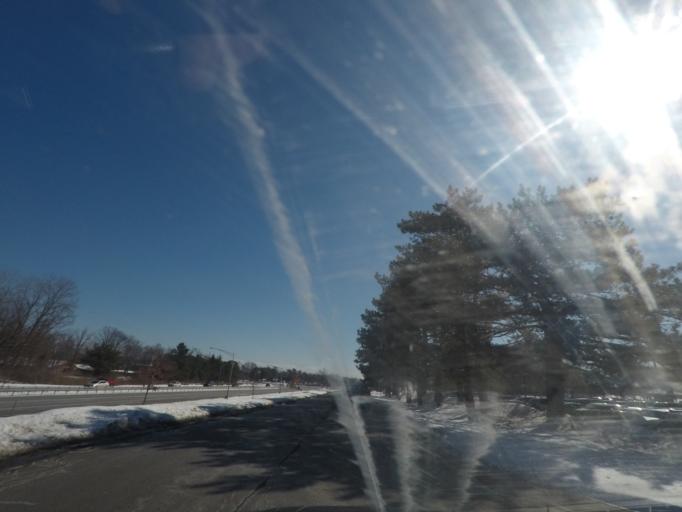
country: US
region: New York
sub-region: Albany County
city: Westmere
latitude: 42.7032
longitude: -73.8559
